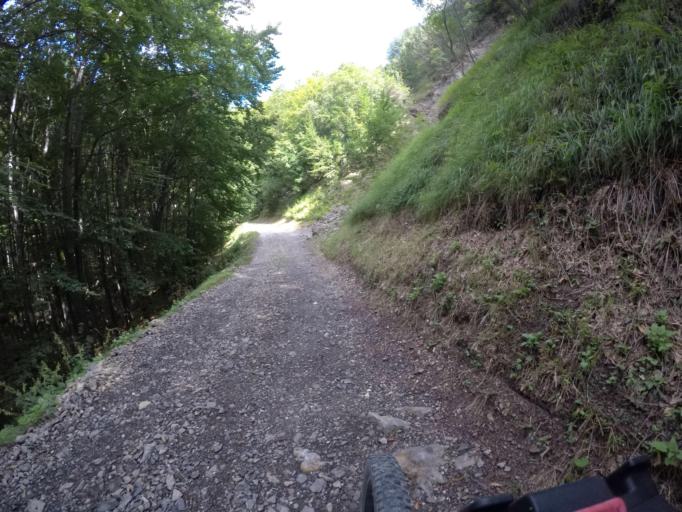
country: IT
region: Friuli Venezia Giulia
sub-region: Provincia di Udine
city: Moggio Udinese
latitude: 46.4862
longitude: 13.1838
